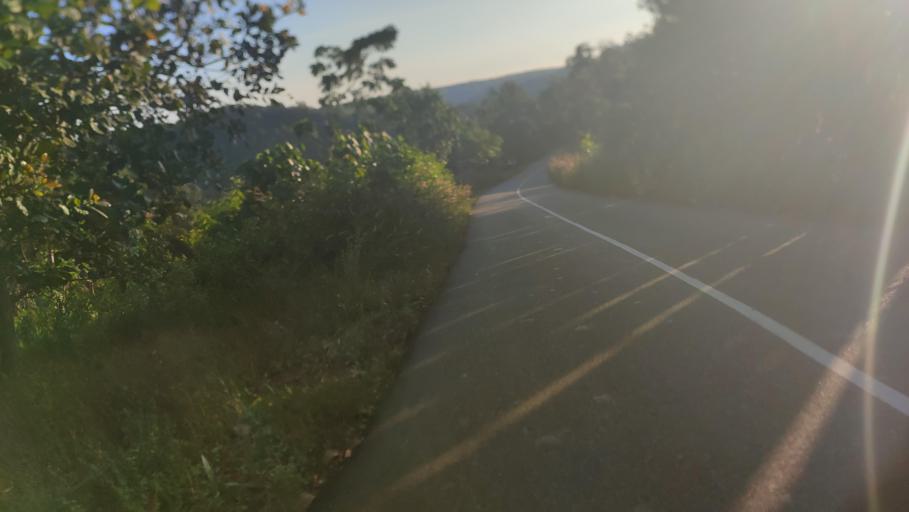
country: IN
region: Kerala
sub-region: Kasaragod District
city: Kasaragod
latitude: 12.4433
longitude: 75.0983
